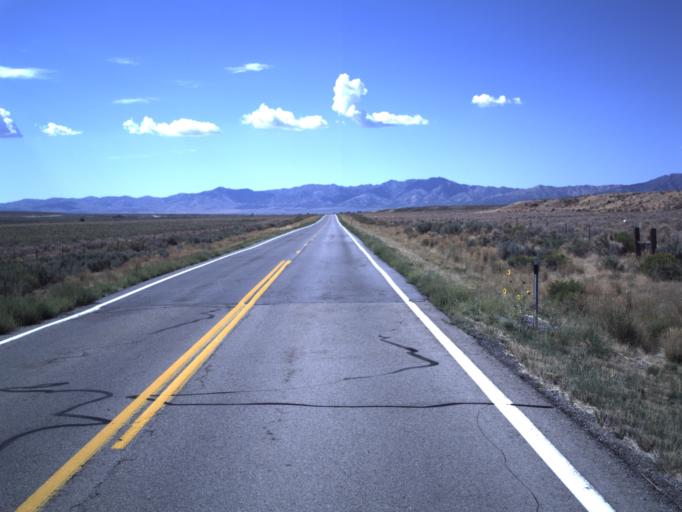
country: US
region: Utah
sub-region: Tooele County
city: Tooele
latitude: 40.2087
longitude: -112.4085
